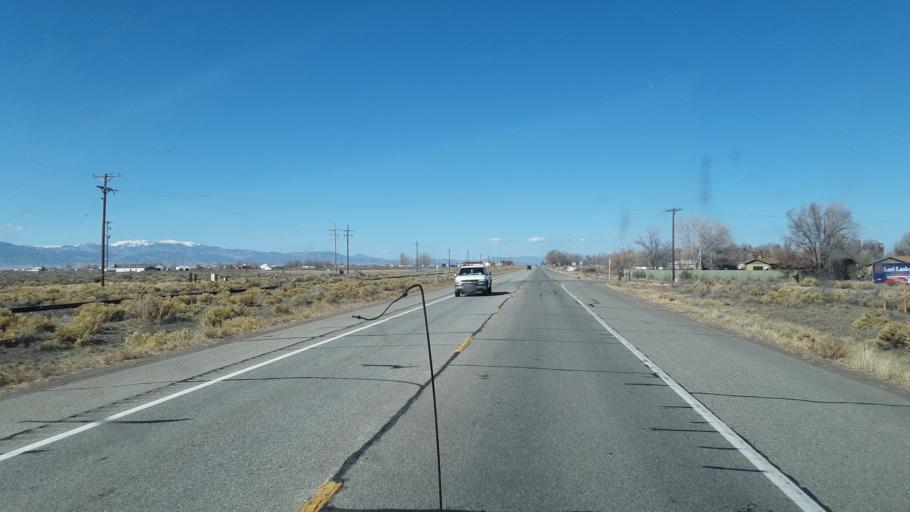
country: US
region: Colorado
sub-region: Alamosa County
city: Alamosa
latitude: 37.4944
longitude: -105.9396
